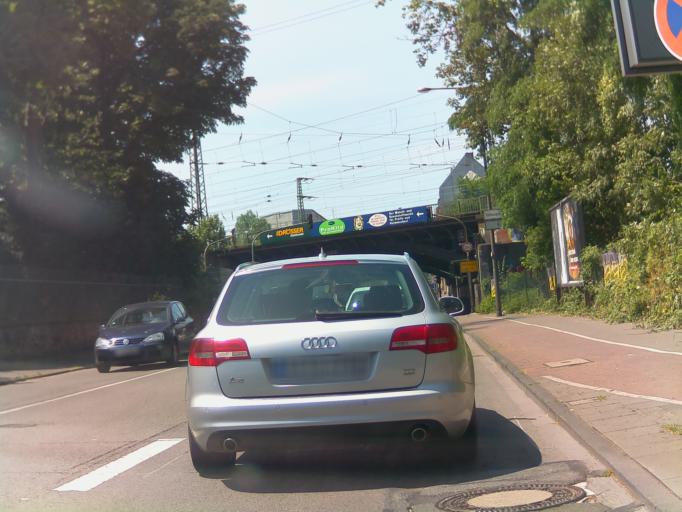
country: DE
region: North Rhine-Westphalia
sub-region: Regierungsbezirk Koln
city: Buchheim
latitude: 50.9643
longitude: 7.0198
